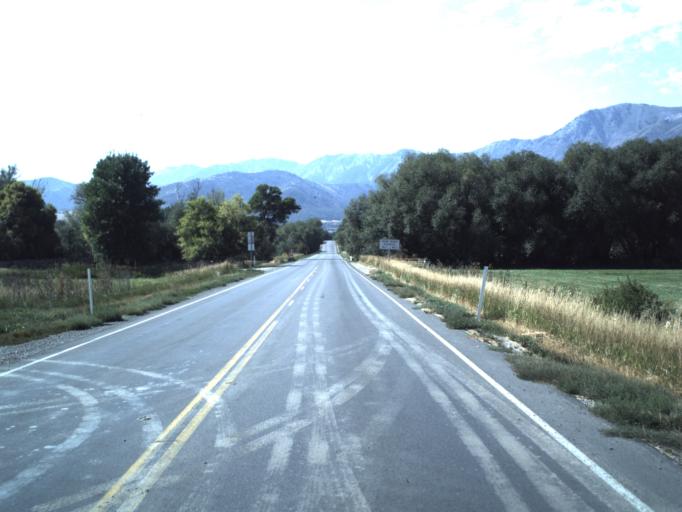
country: US
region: Utah
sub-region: Cache County
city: Wellsville
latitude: 41.6444
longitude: -111.9160
